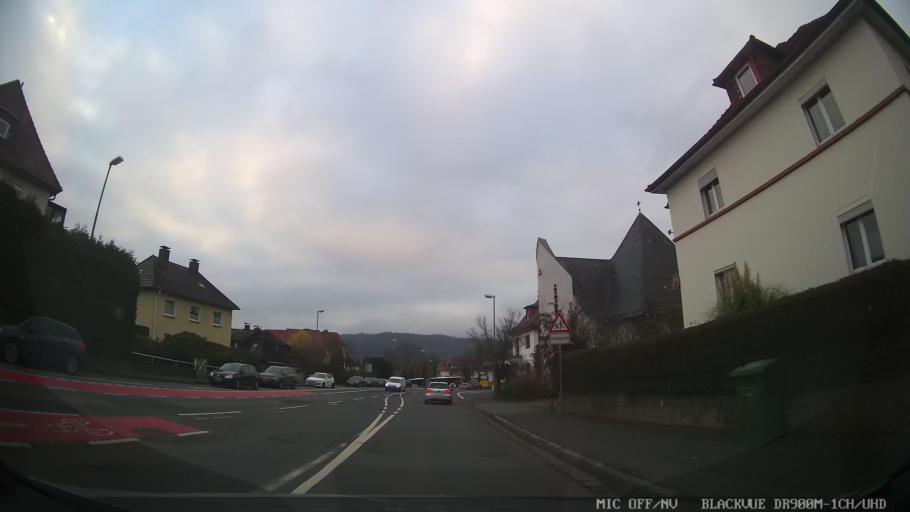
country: DE
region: Hesse
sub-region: Regierungsbezirk Giessen
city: Marburg an der Lahn
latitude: 50.7969
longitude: 8.7679
